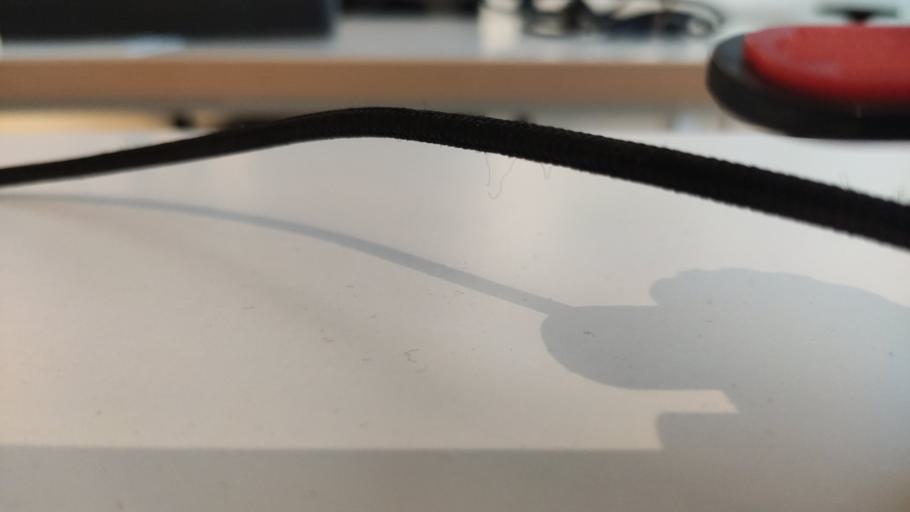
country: RU
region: Moskovskaya
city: Novopetrovskoye
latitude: 55.9639
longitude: 36.4402
